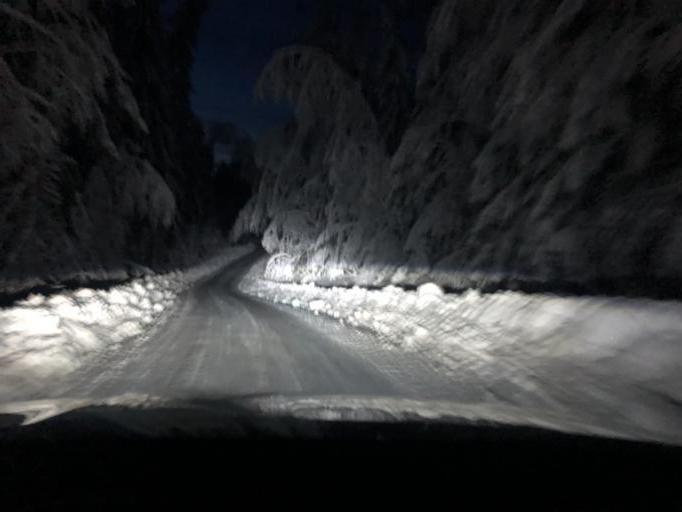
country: SE
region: Vaesternorrland
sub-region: Kramfors Kommun
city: Bollstabruk
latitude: 63.0534
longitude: 17.6838
